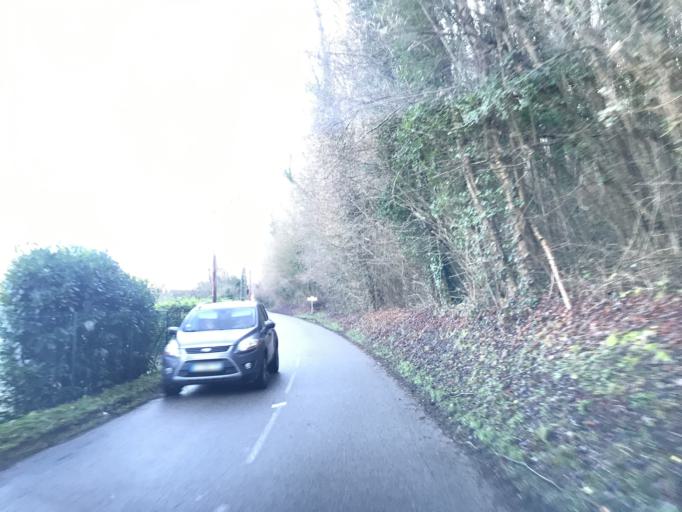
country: FR
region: Haute-Normandie
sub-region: Departement de l'Eure
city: Saint-Aubin-sur-Gaillon
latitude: 49.0899
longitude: 1.2632
